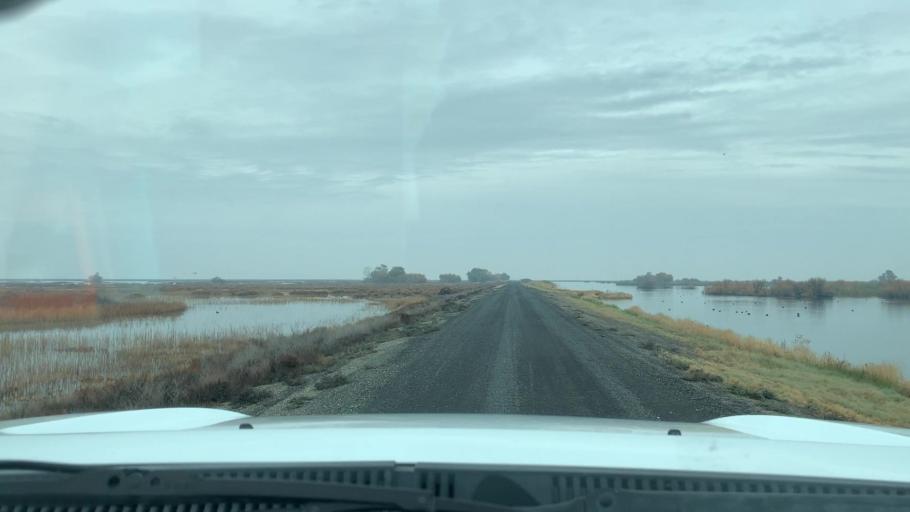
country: US
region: California
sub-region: Kern County
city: Lost Hills
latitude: 35.7498
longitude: -119.5917
